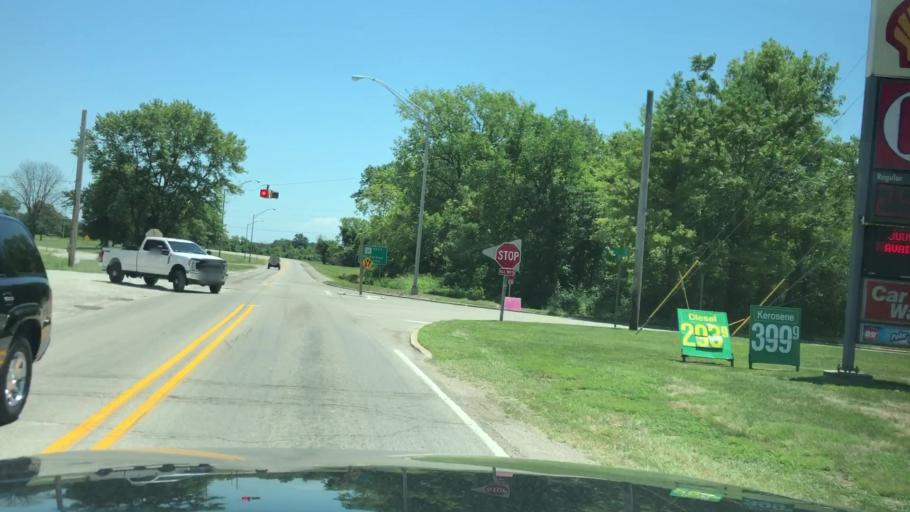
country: US
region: Illinois
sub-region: Saint Clair County
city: Alorton
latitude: 38.5478
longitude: -90.0713
